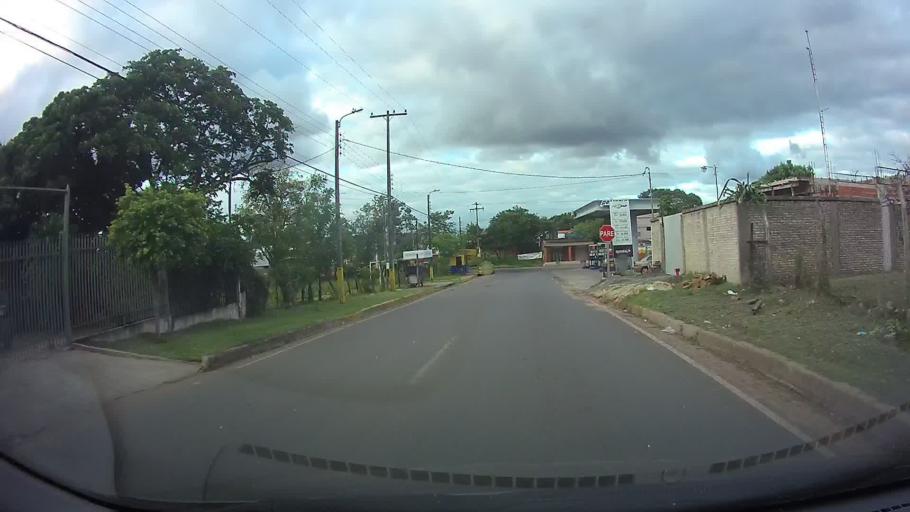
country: PY
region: Central
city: Fernando de la Mora
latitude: -25.2971
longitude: -57.5196
